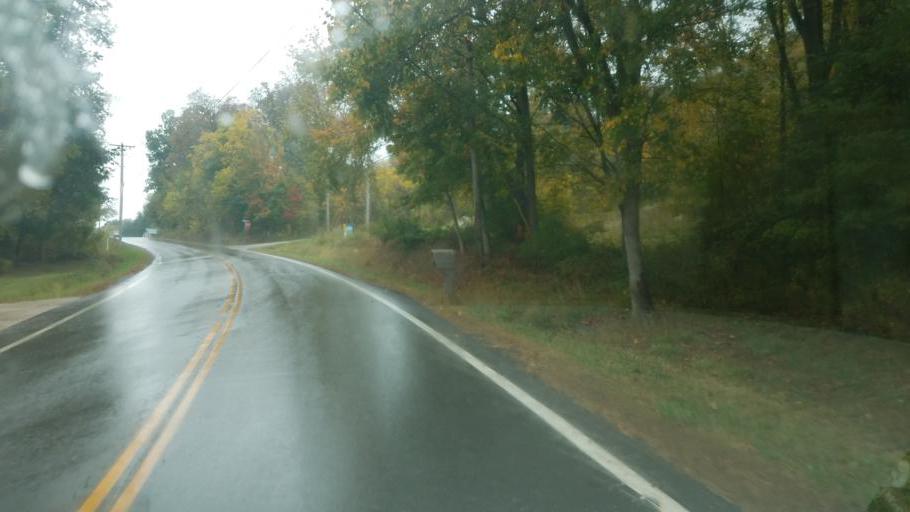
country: US
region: Ohio
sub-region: Richland County
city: Lincoln Heights
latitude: 40.7201
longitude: -82.3748
